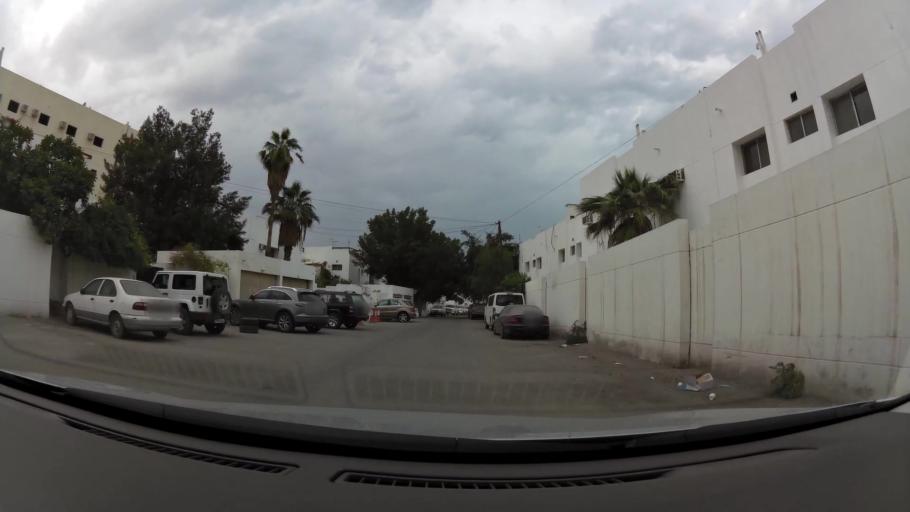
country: QA
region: Baladiyat ad Dawhah
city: Doha
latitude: 25.2748
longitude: 51.5031
